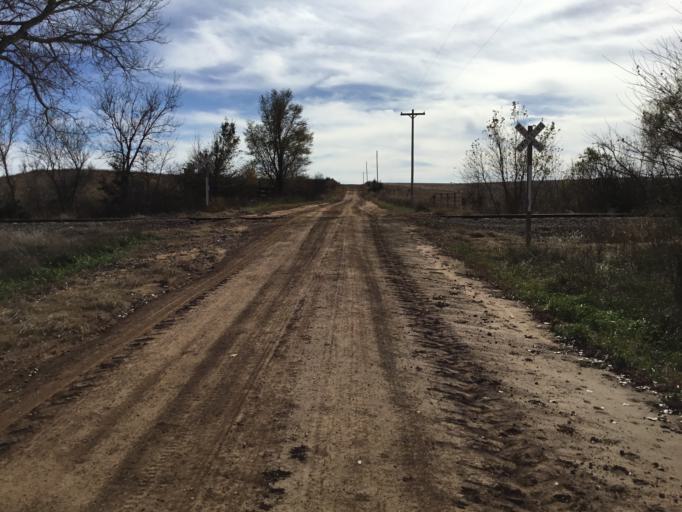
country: US
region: Kansas
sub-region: Lincoln County
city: Lincoln
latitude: 38.9113
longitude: -97.9847
